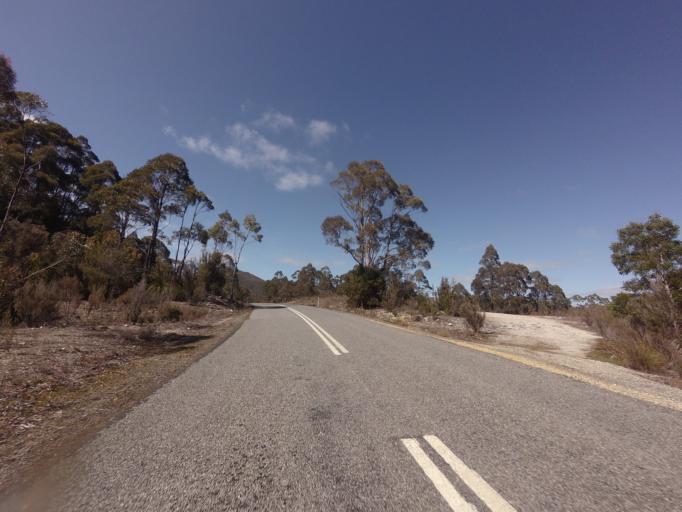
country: AU
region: Tasmania
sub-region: Huon Valley
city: Geeveston
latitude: -42.7715
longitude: 146.3969
